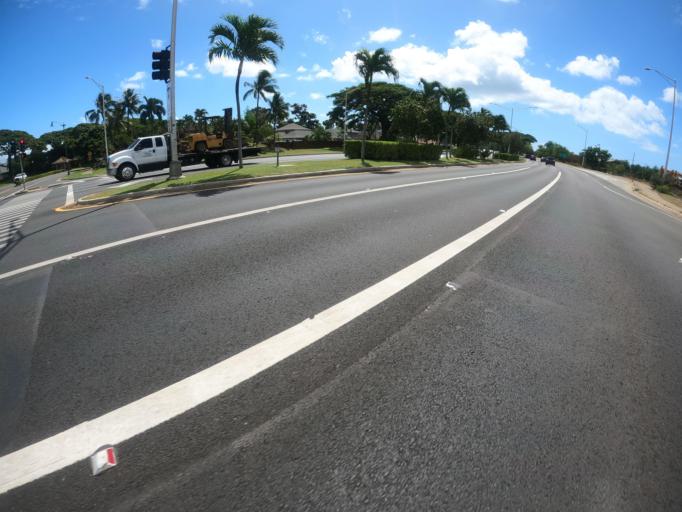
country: US
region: Hawaii
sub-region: Honolulu County
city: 'Ewa Gentry
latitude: 21.3603
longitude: -158.0294
